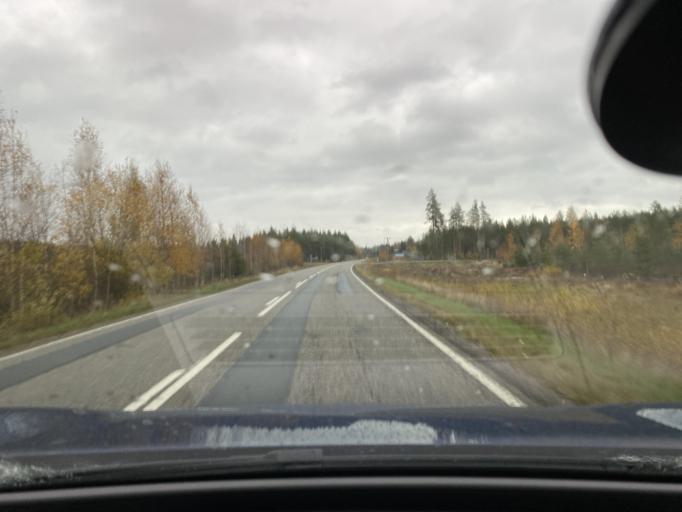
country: FI
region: Satakunta
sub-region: Rauma
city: Saekylae
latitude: 61.0465
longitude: 22.4201
